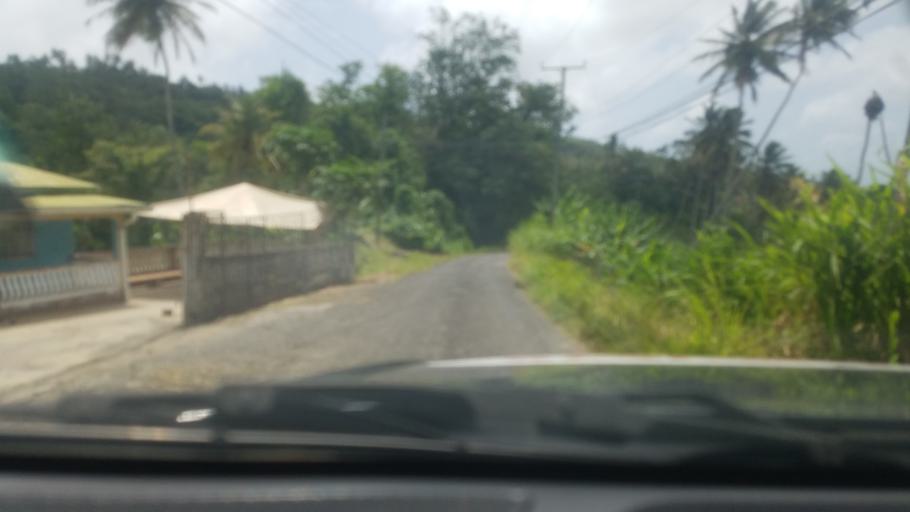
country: LC
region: Micoud Quarter
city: Micoud
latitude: 13.7989
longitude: -60.9476
